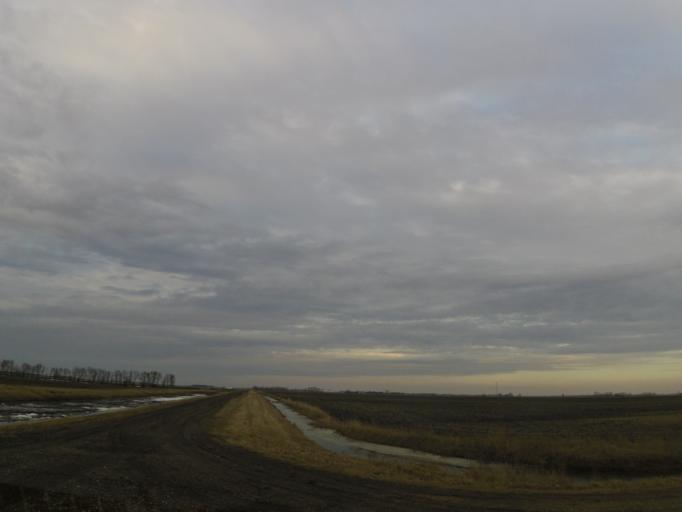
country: US
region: North Dakota
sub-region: Walsh County
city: Grafton
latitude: 48.3685
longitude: -97.2112
